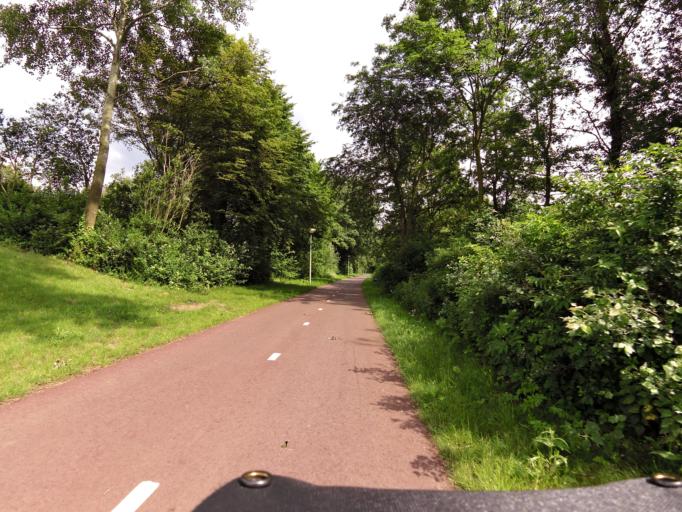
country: NL
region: South Holland
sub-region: Gemeente Maassluis
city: Maassluis
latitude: 51.9091
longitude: 4.2474
